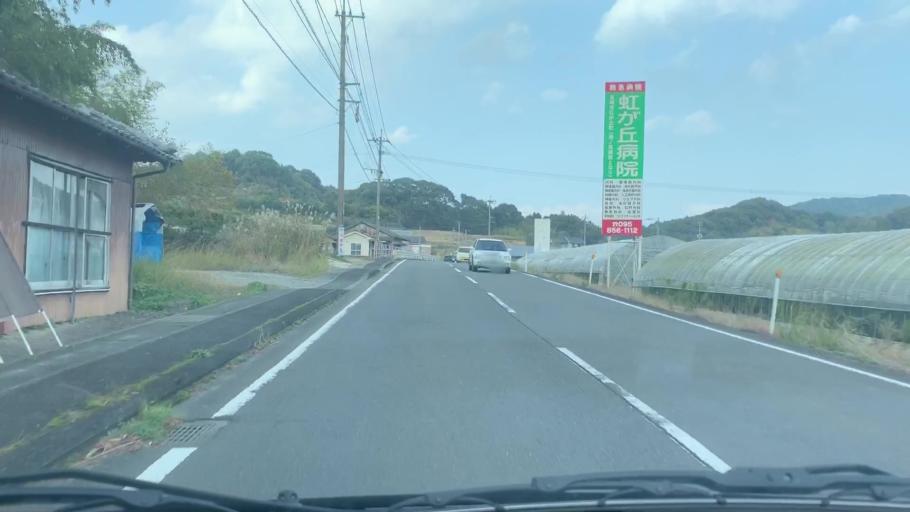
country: JP
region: Nagasaki
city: Togitsu
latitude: 32.9673
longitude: 129.7809
